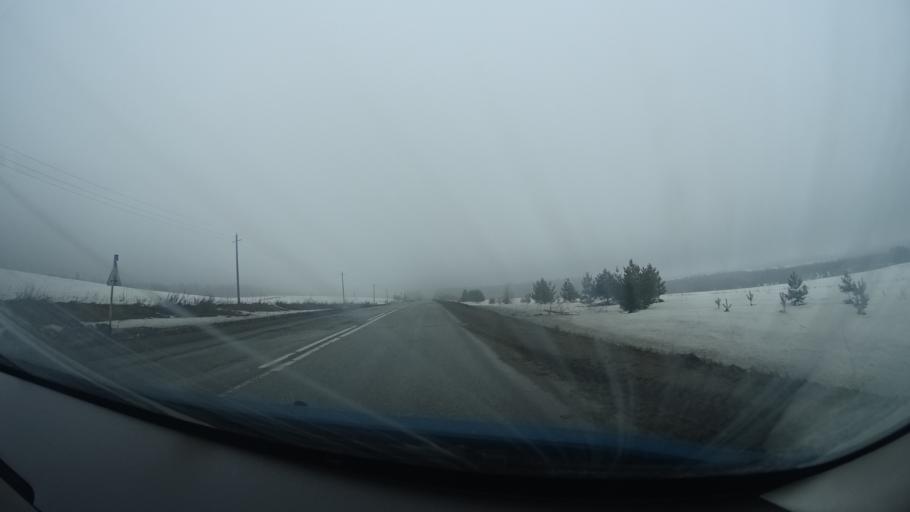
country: RU
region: Perm
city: Kuyeda
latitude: 56.4715
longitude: 55.7447
